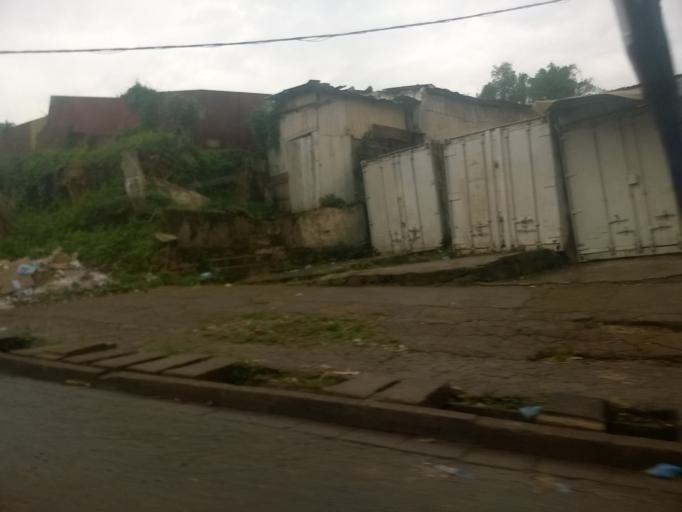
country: CM
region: Centre
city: Yaounde
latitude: 3.8677
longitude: 11.5183
